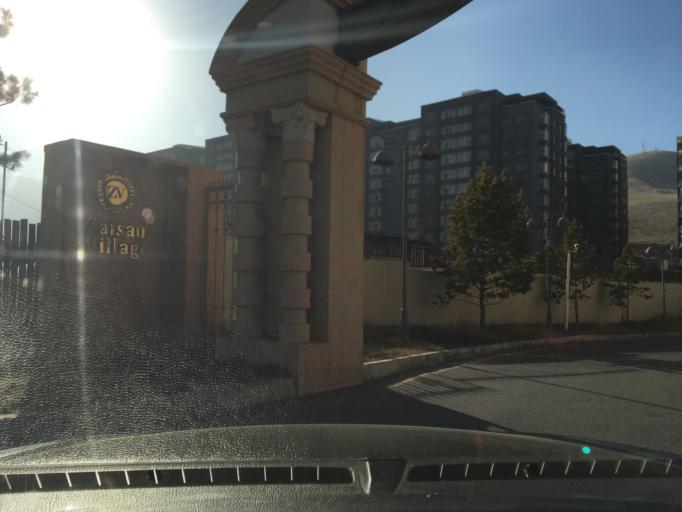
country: MN
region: Ulaanbaatar
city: Ulaanbaatar
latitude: 47.8753
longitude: 106.9108
